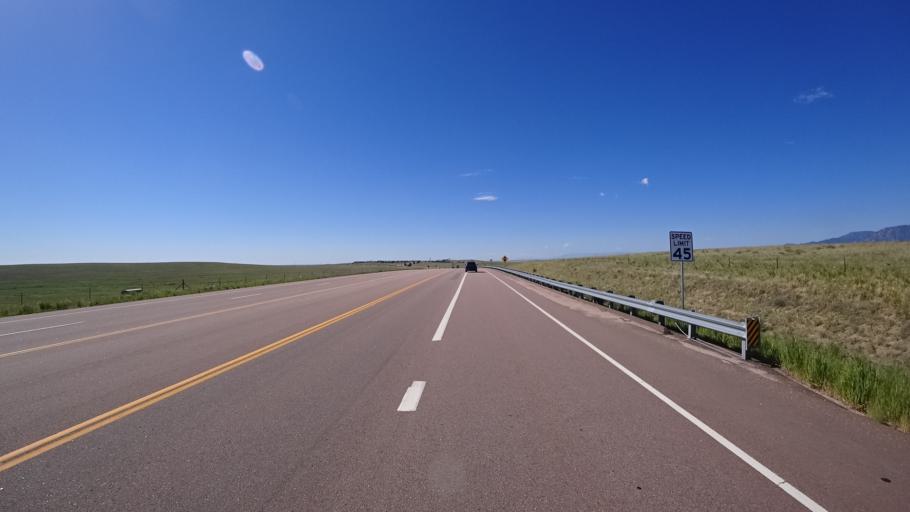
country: US
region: Colorado
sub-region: El Paso County
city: Cimarron Hills
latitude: 38.8299
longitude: -104.6827
